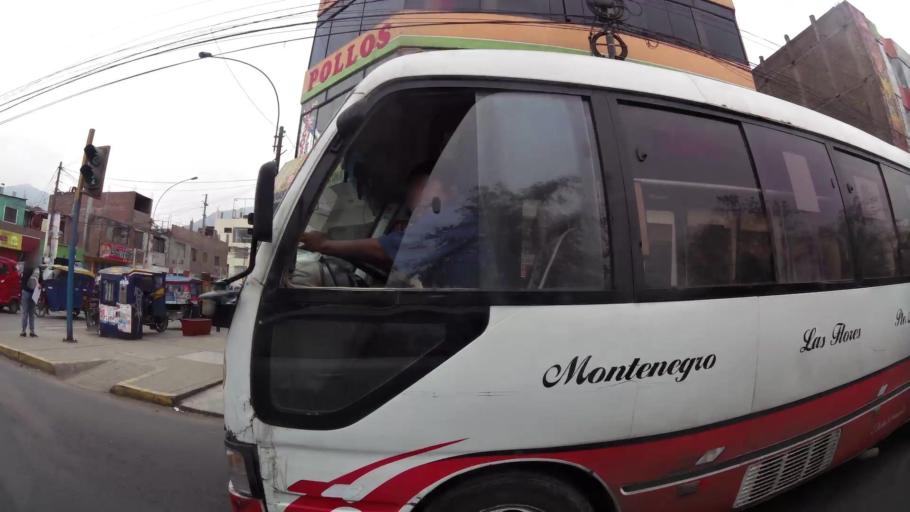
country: PE
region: Lima
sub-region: Lima
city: Independencia
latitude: -11.9752
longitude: -77.0089
